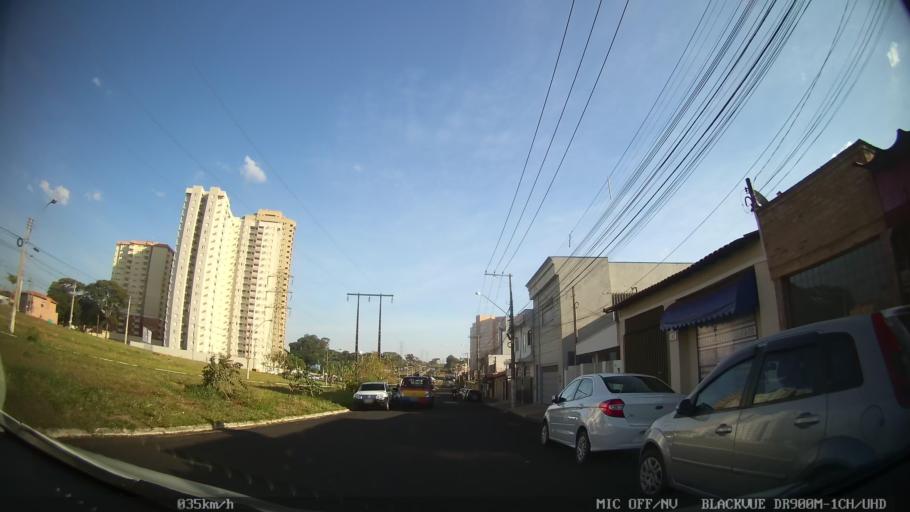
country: BR
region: Sao Paulo
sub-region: Ribeirao Preto
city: Ribeirao Preto
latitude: -21.1956
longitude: -47.7783
